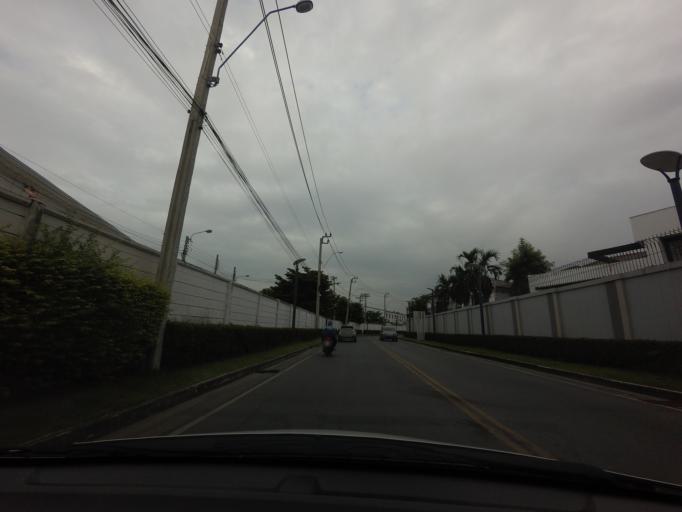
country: TH
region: Bangkok
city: Suan Luang
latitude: 13.7200
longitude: 100.6302
